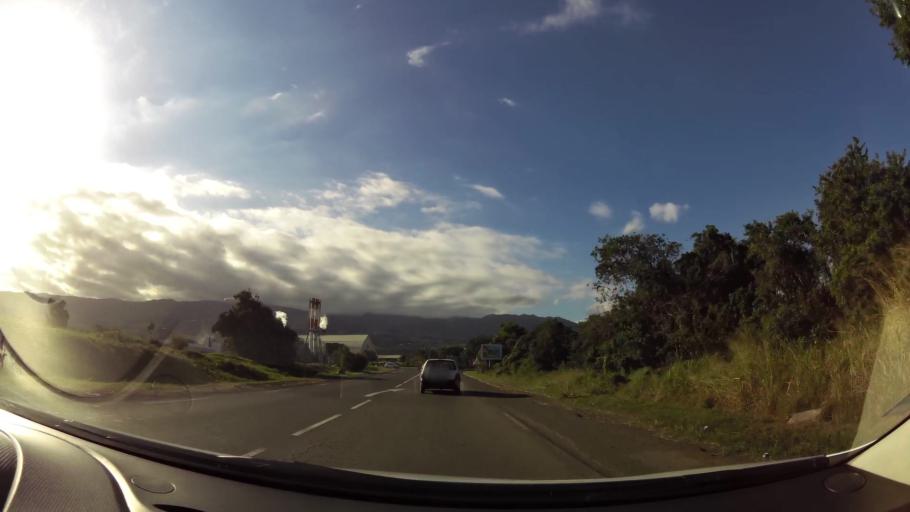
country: RE
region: Reunion
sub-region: Reunion
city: Saint-Louis
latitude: -21.2839
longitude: 55.3980
